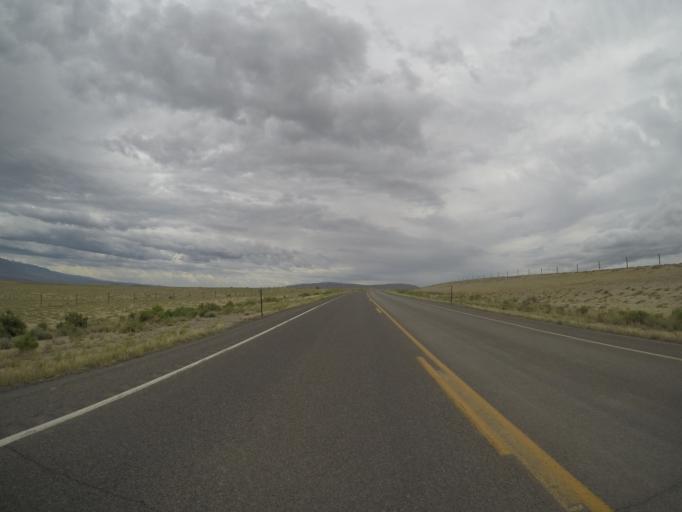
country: US
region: Wyoming
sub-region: Big Horn County
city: Lovell
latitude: 44.8927
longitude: -108.2887
